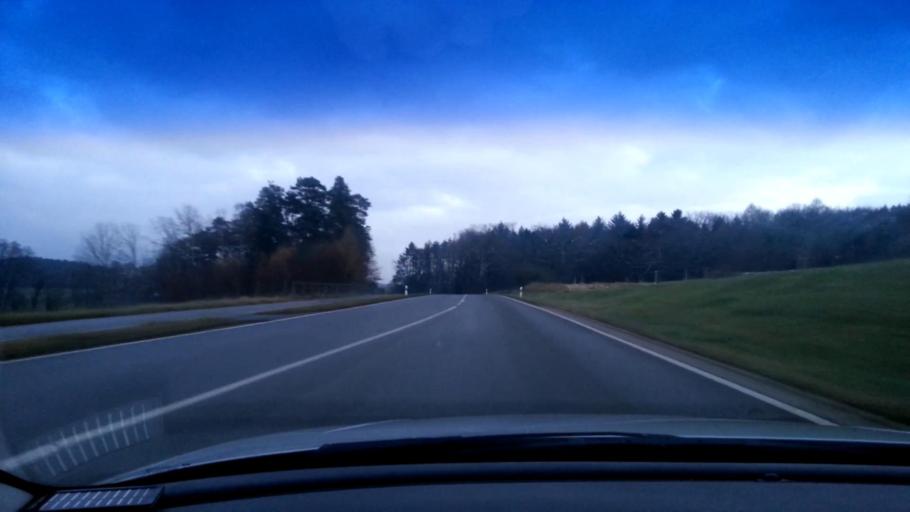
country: DE
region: Bavaria
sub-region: Upper Franconia
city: Pettstadt
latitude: 49.8428
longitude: 10.9161
